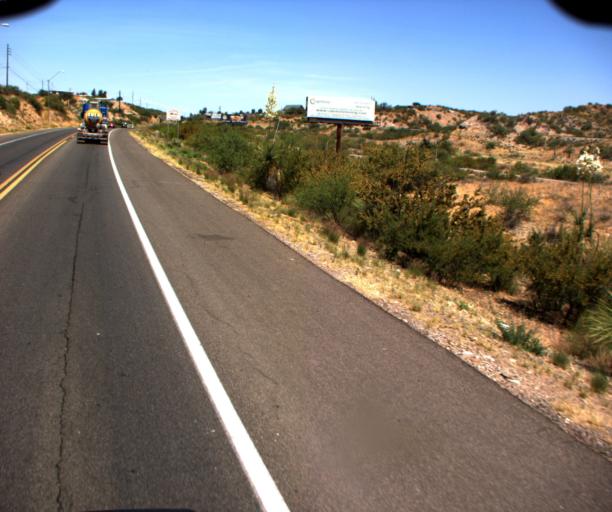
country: US
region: Arizona
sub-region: Gila County
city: Globe
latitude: 33.3743
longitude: -110.7405
